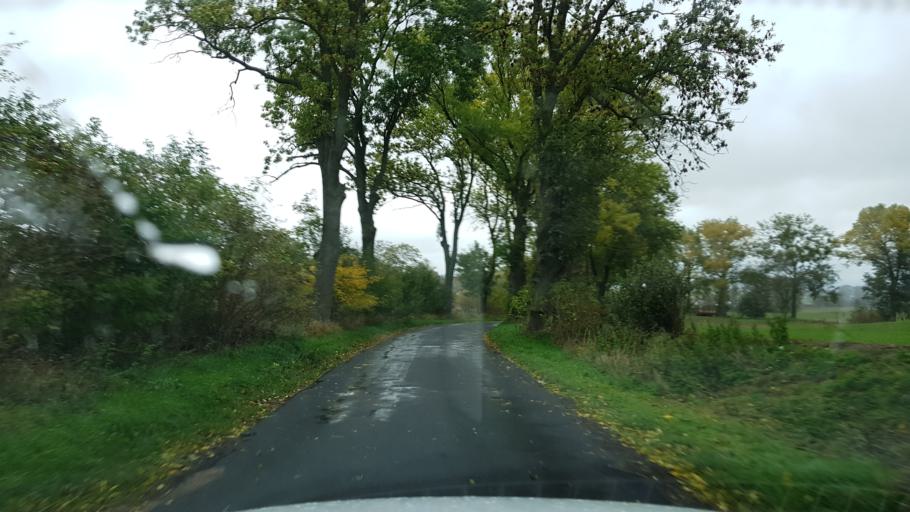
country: PL
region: West Pomeranian Voivodeship
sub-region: Powiat pyrzycki
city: Kozielice
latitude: 53.0649
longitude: 14.8920
